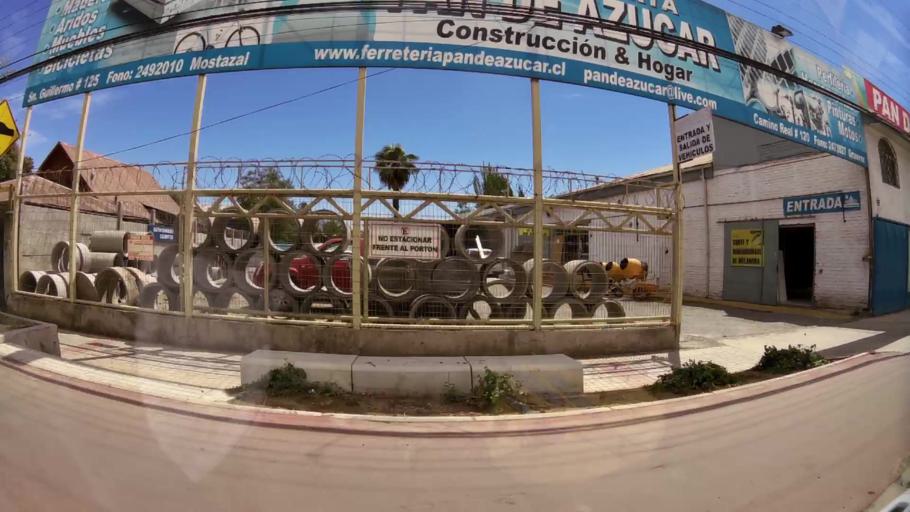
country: CL
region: O'Higgins
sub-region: Provincia de Cachapoal
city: Graneros
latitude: -33.9823
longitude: -70.7115
